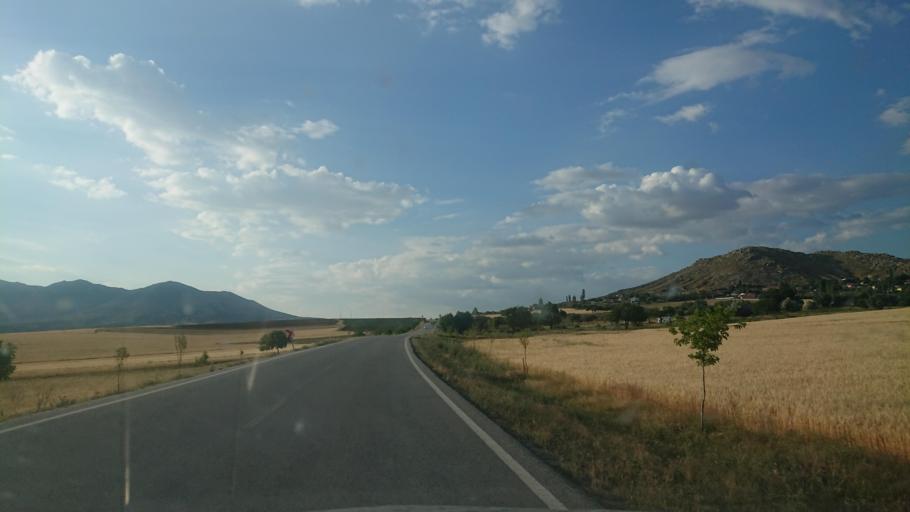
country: TR
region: Aksaray
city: Balci
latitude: 38.5849
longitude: 34.1027
